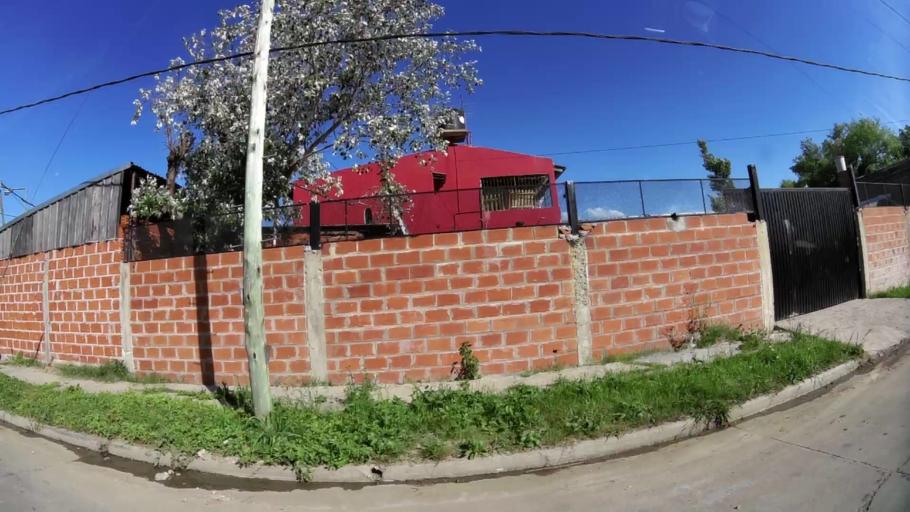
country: AR
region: Buenos Aires
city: Hurlingham
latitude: -34.5510
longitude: -58.6080
